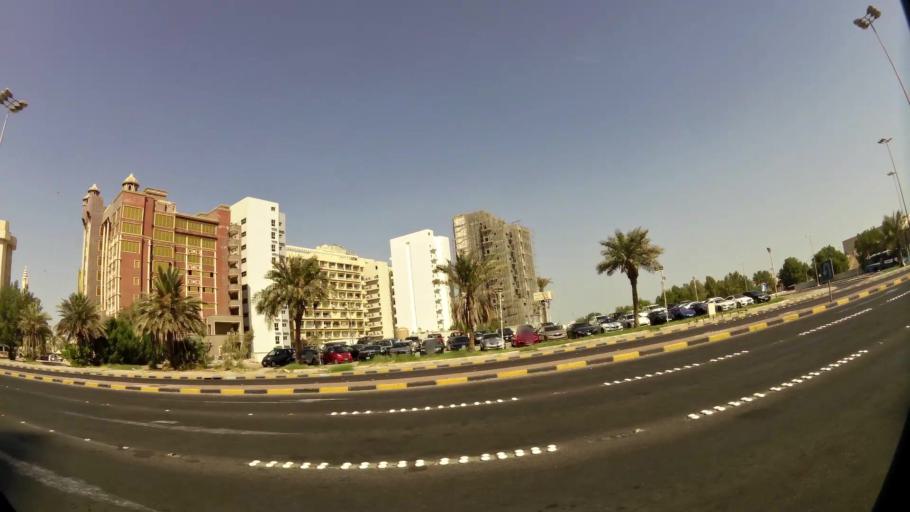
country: KW
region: Muhafazat Hawalli
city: As Salimiyah
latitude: 29.3466
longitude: 48.0946
